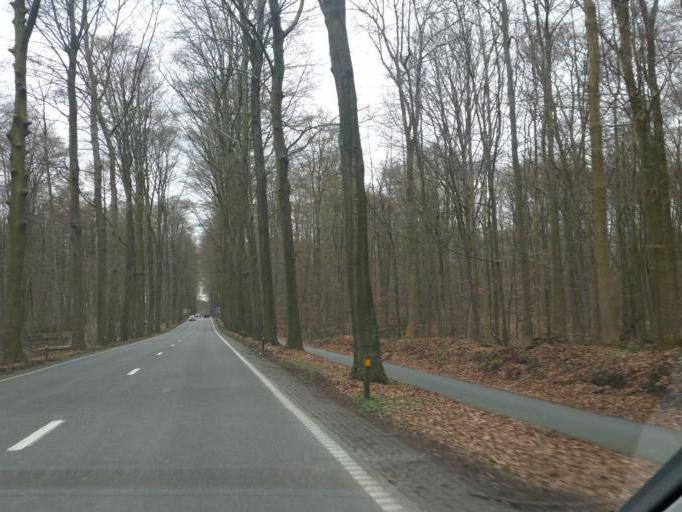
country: BE
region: Flanders
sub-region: Provincie Vlaams-Brabant
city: Sint-Genesius-Rode
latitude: 50.7791
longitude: 4.3888
